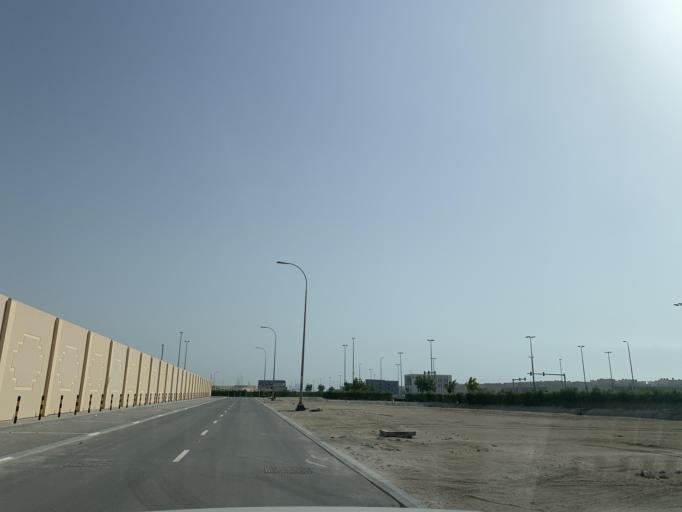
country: BH
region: Muharraq
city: Al Muharraq
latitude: 26.3108
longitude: 50.6326
